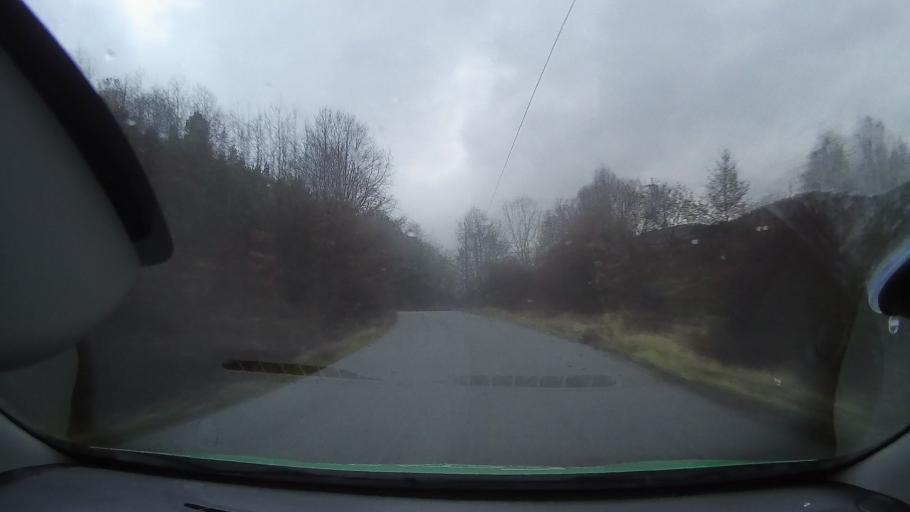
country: RO
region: Hunedoara
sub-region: Comuna Baia de Cris
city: Baia de Cris
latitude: 46.2071
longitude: 22.7159
